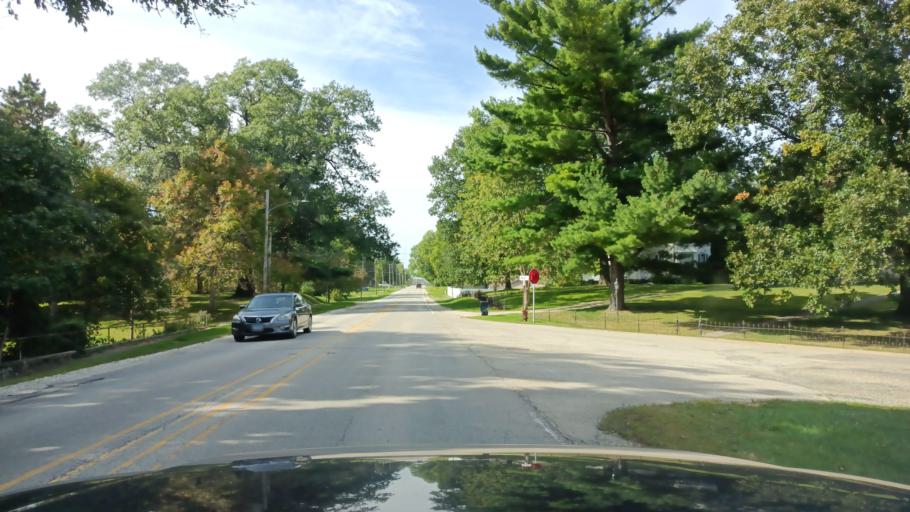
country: US
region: Illinois
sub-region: Knox County
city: Knoxville
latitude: 40.9090
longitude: -90.2910
